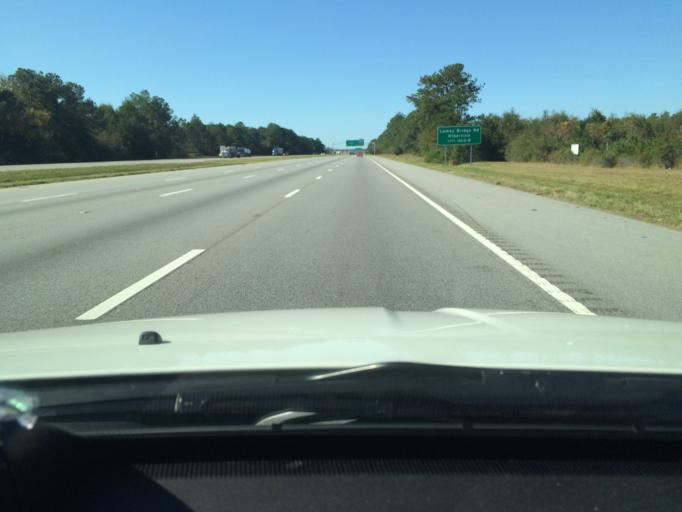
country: US
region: Mississippi
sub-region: Jackson County
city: Saint Martin
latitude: 30.4542
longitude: -88.8716
